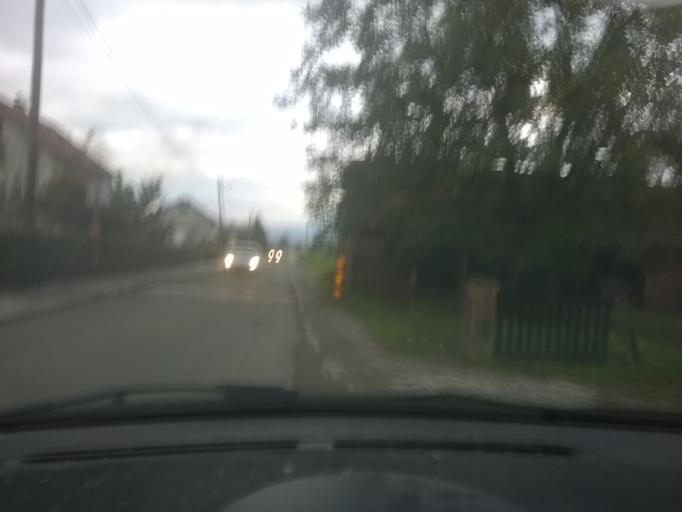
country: HR
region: Zagrebacka
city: Jakovlje
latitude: 45.9959
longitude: 15.8484
